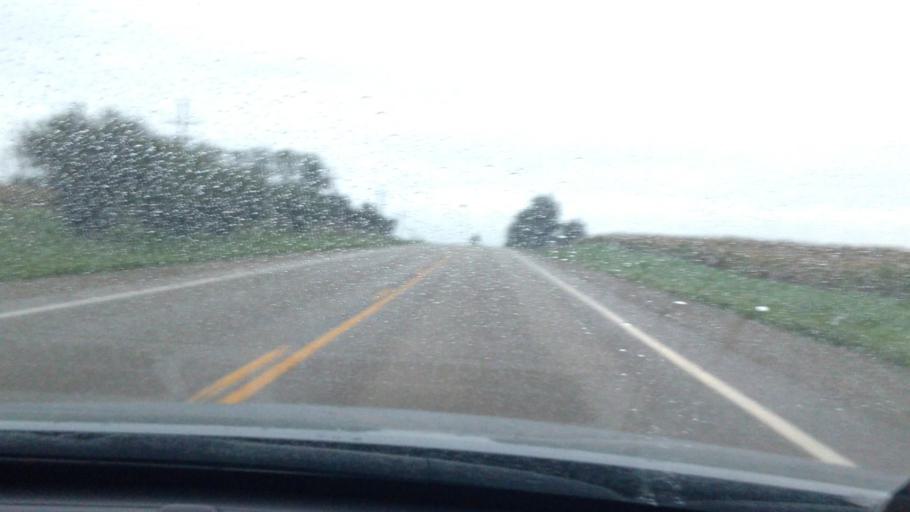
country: US
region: Kansas
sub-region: Brown County
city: Hiawatha
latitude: 39.8182
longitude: -95.5273
